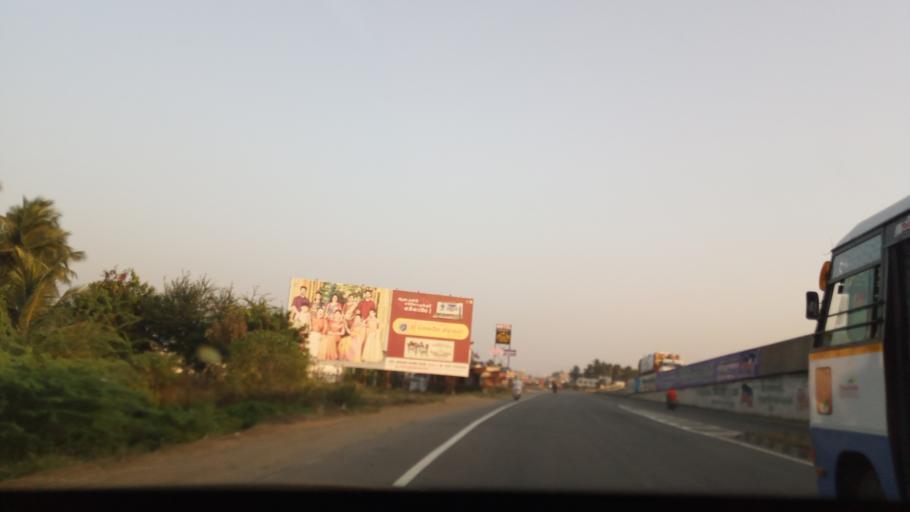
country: IN
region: Tamil Nadu
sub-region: Salem
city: Omalur
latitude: 11.7358
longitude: 78.0535
